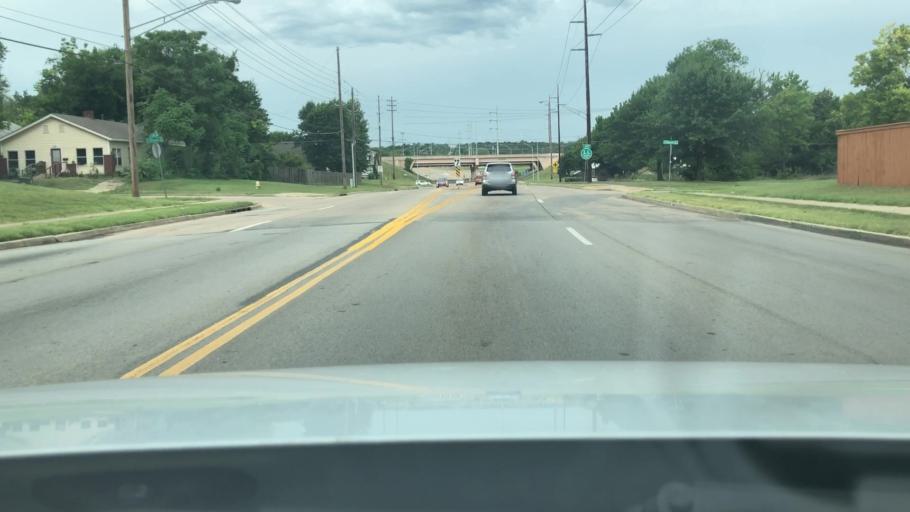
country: US
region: Oklahoma
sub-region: Tulsa County
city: Tulsa
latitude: 36.1770
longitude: -95.9975
